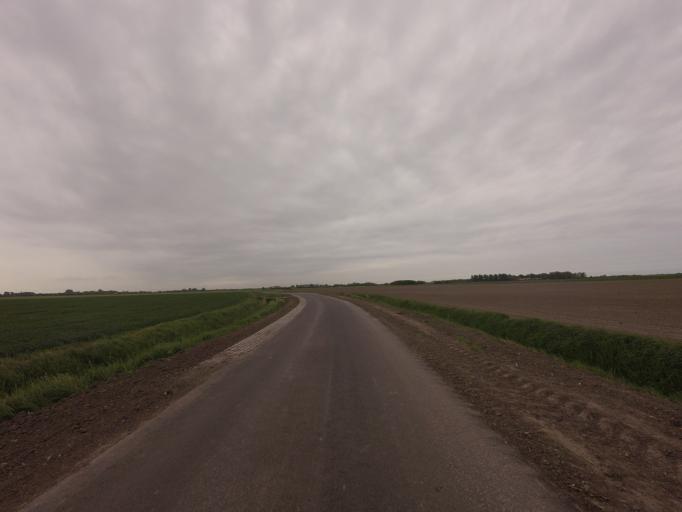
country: NL
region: Zeeland
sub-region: Gemeente Middelburg
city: Middelburg
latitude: 51.5475
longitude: 3.5451
